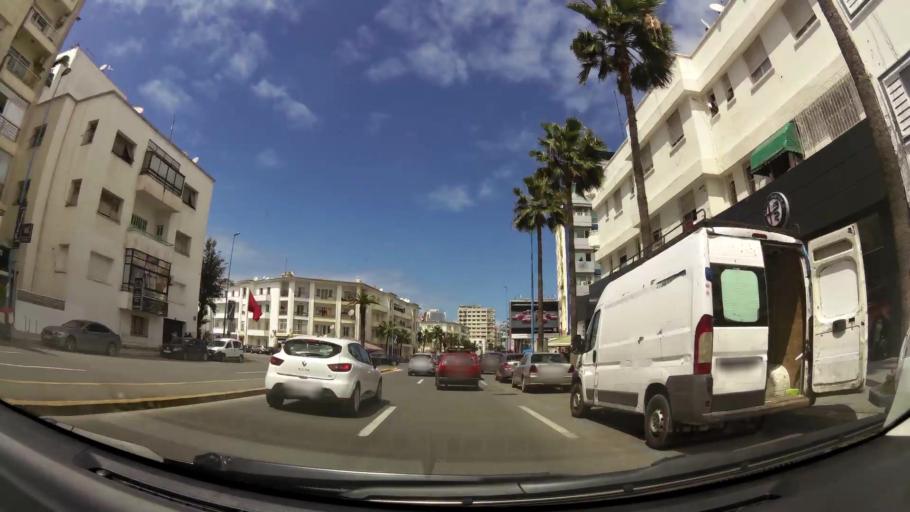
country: MA
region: Grand Casablanca
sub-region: Casablanca
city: Casablanca
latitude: 33.5935
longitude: -7.6375
